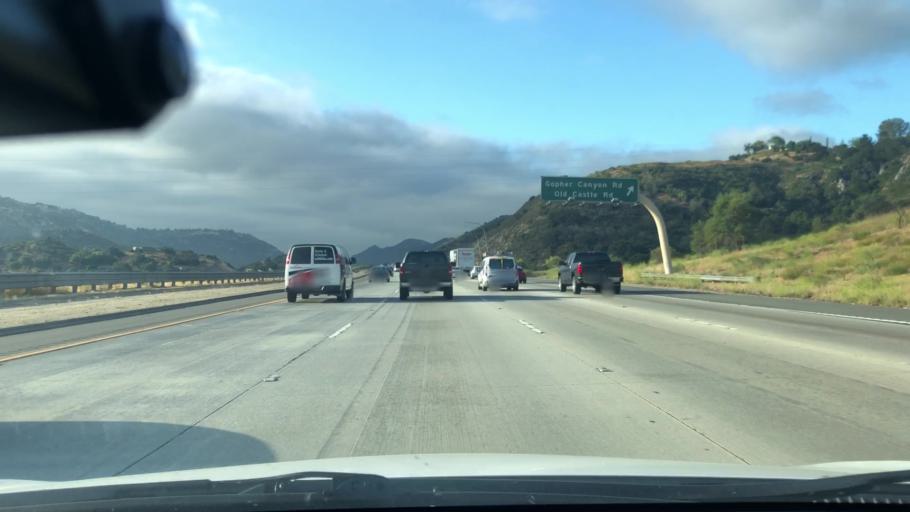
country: US
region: California
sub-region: San Diego County
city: Hidden Meadows
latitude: 33.2568
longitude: -117.1577
